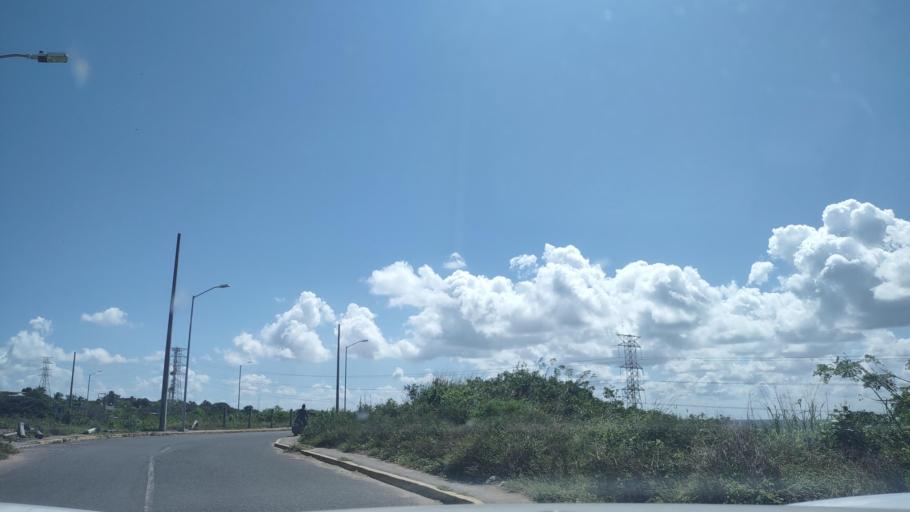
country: MX
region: Veracruz
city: Heroica Alvarado
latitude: 18.7780
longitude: -95.7613
